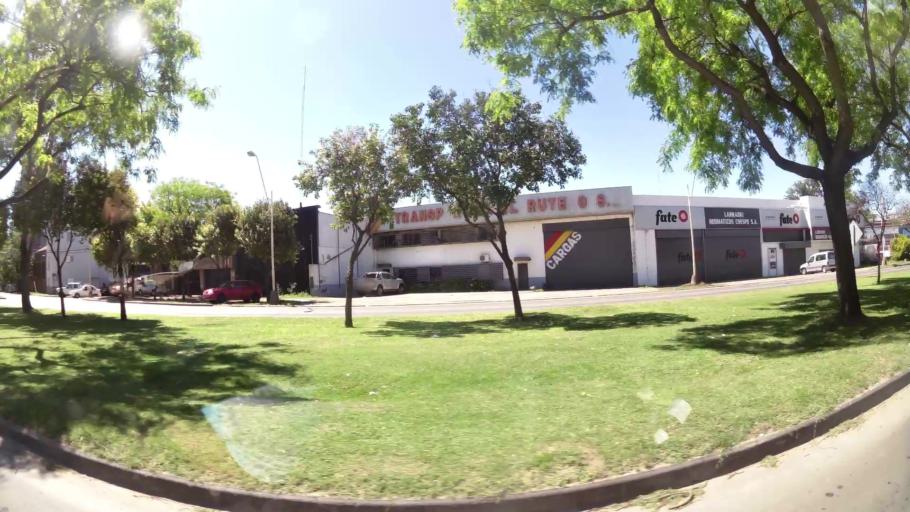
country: AR
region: Santa Fe
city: Santa Fe de la Vera Cruz
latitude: -31.6453
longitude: -60.6951
